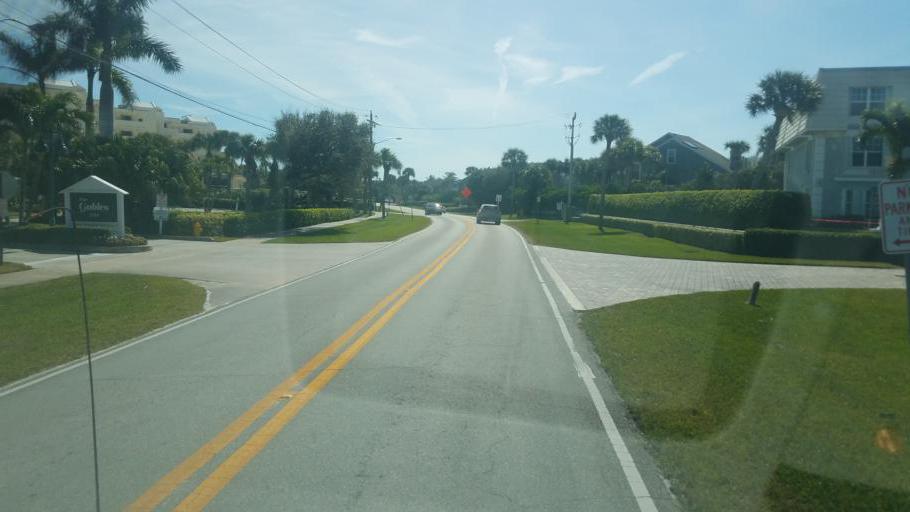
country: US
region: Florida
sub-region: Indian River County
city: Vero Beach
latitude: 27.6471
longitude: -80.3547
